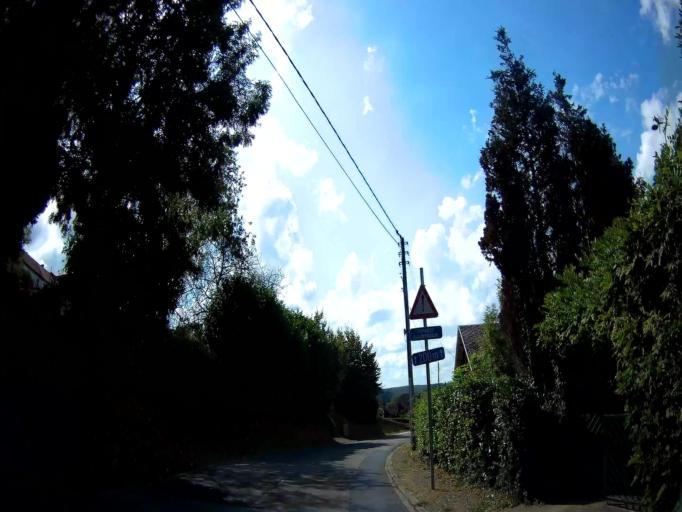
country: BE
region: Wallonia
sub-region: Province de Namur
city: Yvoir
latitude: 50.3486
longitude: 4.8778
